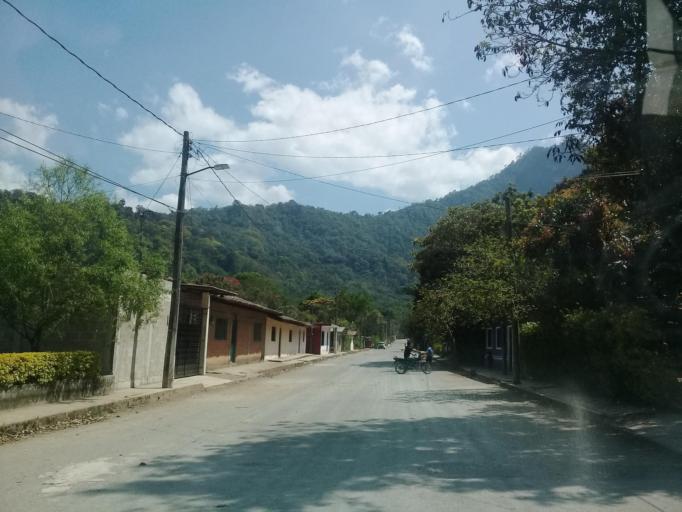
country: MX
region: Veracruz
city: Jalapilla
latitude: 18.8089
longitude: -97.0709
